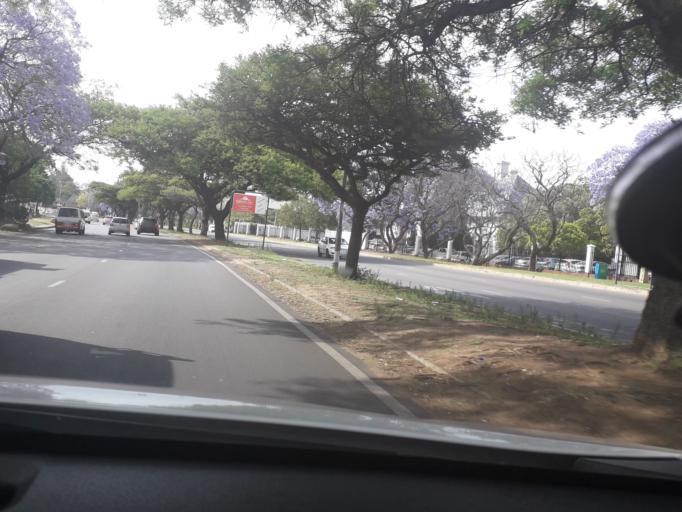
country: ZA
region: Gauteng
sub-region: City of Johannesburg Metropolitan Municipality
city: Diepsloot
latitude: -26.0469
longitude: 28.0200
